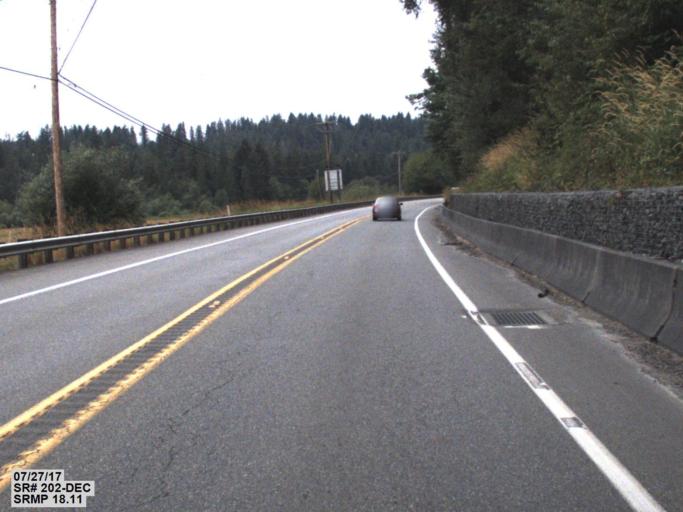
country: US
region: Washington
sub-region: King County
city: Ames Lake
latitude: 47.5897
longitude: -121.9554
